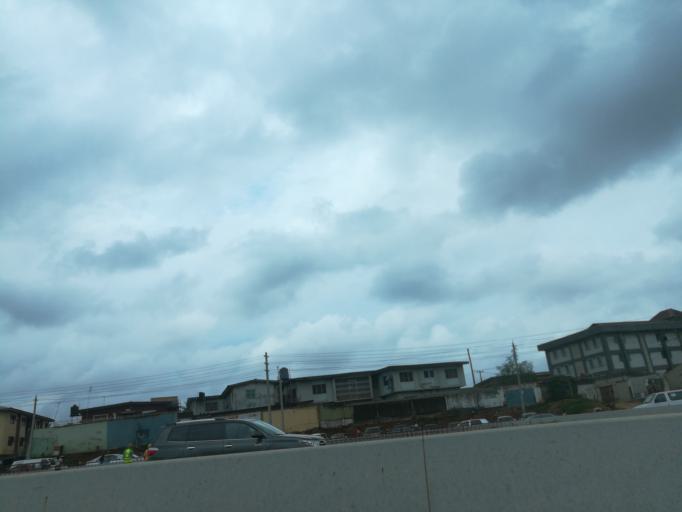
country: NG
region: Lagos
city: Oshodi
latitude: 6.5538
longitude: 3.3260
